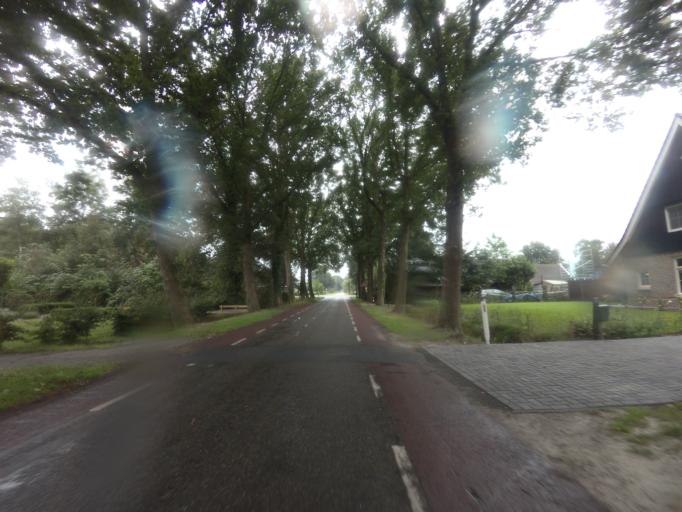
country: NL
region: Drenthe
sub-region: Gemeente Hoogeveen
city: Hoogeveen
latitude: 52.6735
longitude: 6.5368
